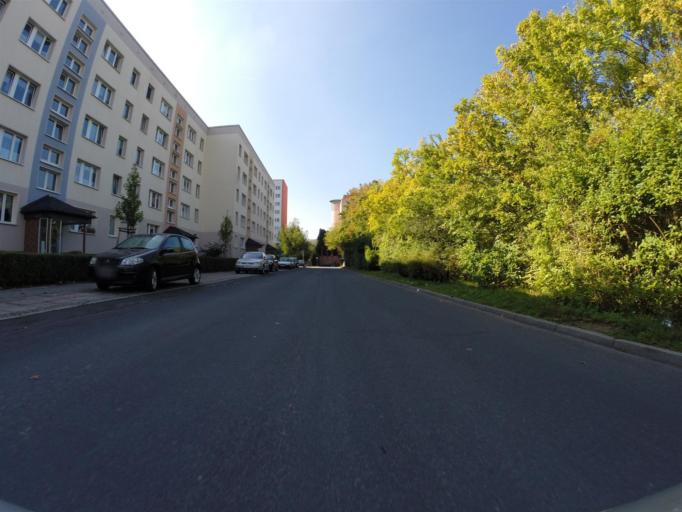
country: DE
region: Thuringia
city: Sulza
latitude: 50.8807
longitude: 11.6018
